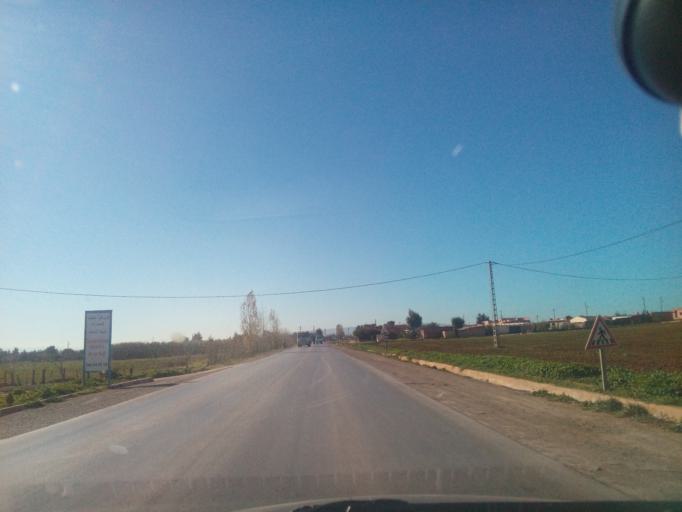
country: DZ
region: Relizane
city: Djidiouia
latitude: 35.8955
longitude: 0.6695
